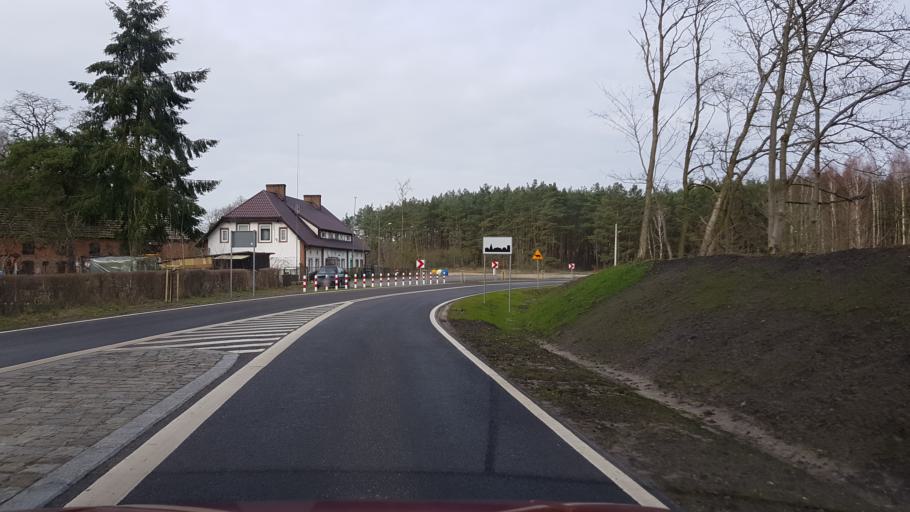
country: PL
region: West Pomeranian Voivodeship
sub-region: Powiat policki
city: Nowe Warpno
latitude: 53.6885
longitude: 14.3551
